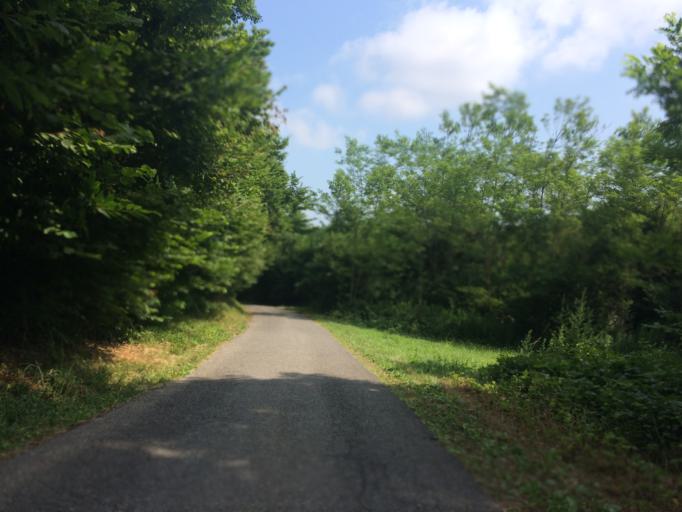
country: IT
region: Liguria
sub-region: Provincia di Savona
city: Giusvalla
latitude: 44.4607
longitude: 8.3550
